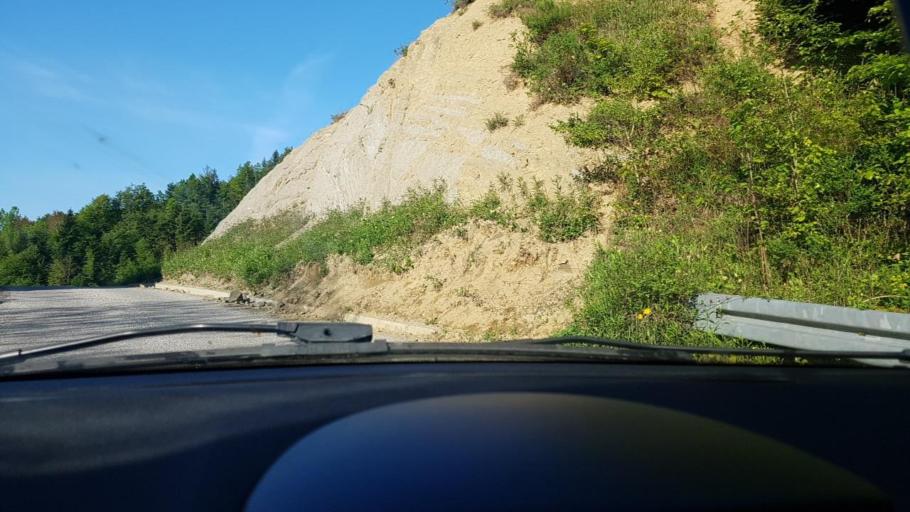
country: SI
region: Zetale
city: Zetale
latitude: 46.2613
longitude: 15.8593
